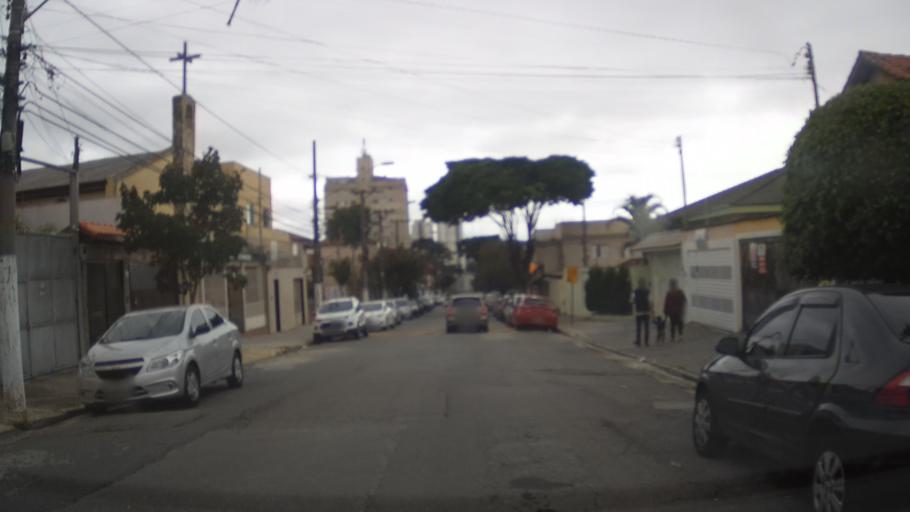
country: BR
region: Sao Paulo
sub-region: Guarulhos
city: Guarulhos
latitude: -23.5210
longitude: -46.5234
